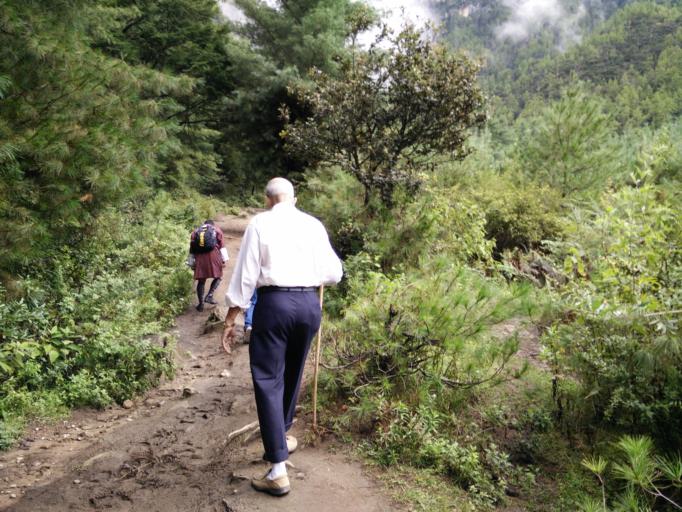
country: BT
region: Paro
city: Paro
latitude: 27.4832
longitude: 89.3611
